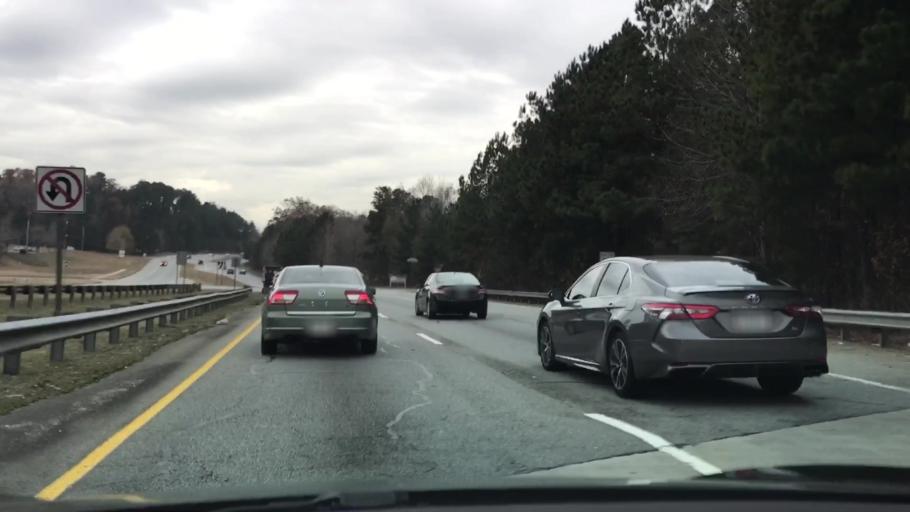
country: US
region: Georgia
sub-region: Gwinnett County
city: Suwanee
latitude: 34.0322
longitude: -84.1076
